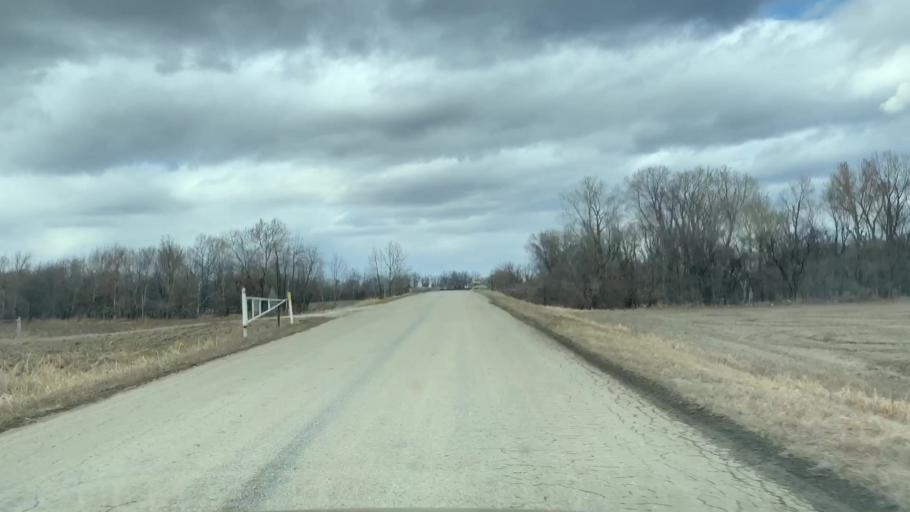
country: US
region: Kansas
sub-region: Allen County
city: Humboldt
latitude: 37.8030
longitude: -95.4709
